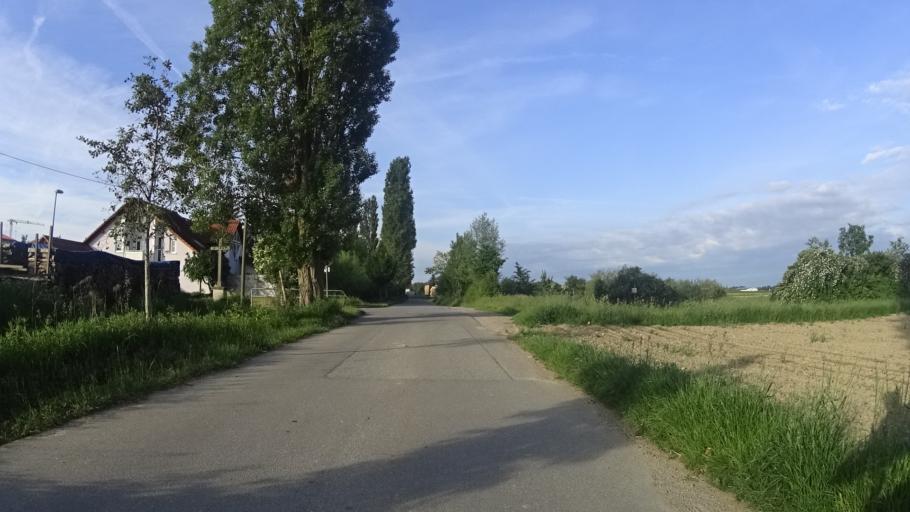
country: DE
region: Baden-Wuerttemberg
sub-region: Freiburg Region
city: Hartheim
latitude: 47.9411
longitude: 7.6480
